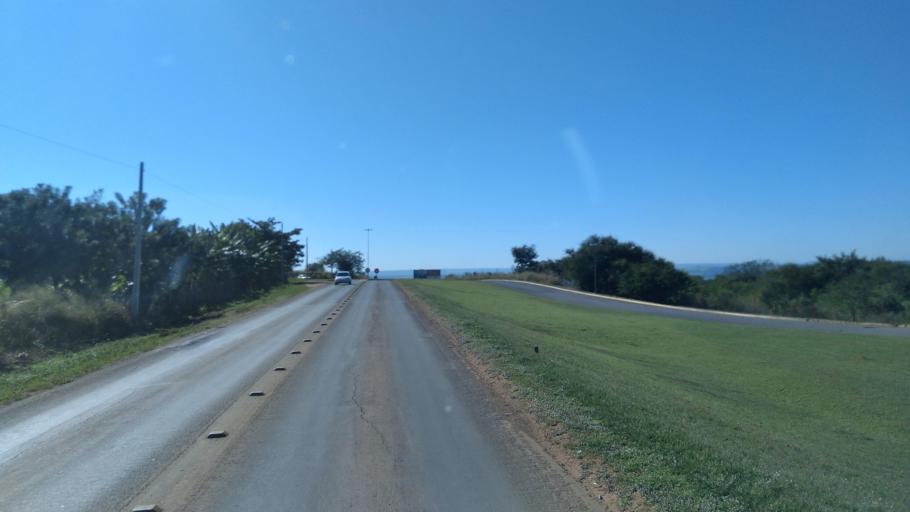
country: BR
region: Goias
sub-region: Mineiros
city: Mineiros
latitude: -17.5788
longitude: -52.5377
